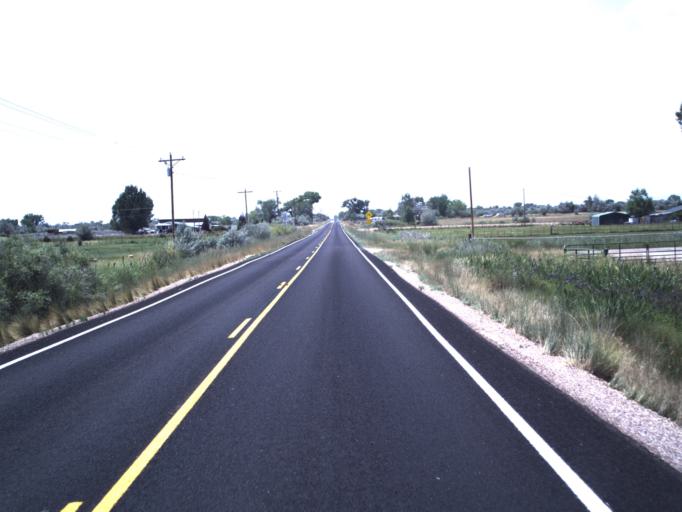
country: US
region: Utah
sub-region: Duchesne County
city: Roosevelt
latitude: 40.4037
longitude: -109.8567
